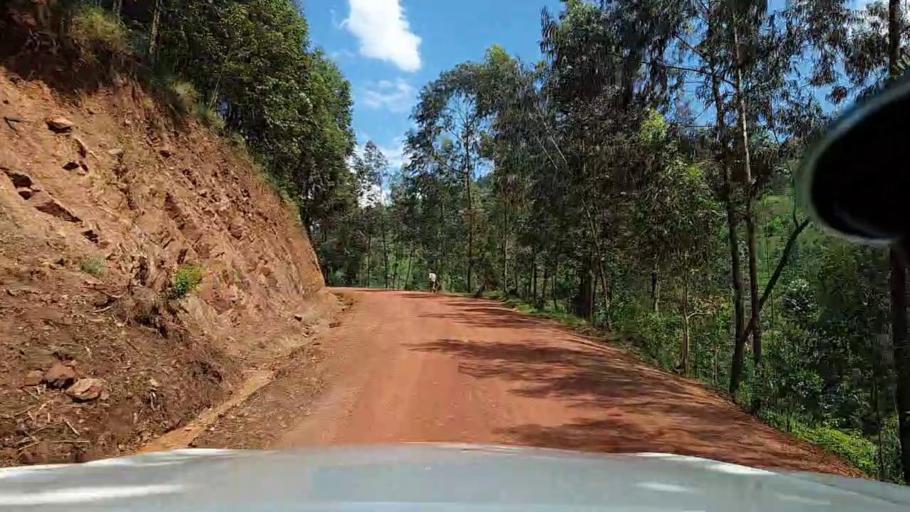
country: RW
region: Northern Province
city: Byumba
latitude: -1.7454
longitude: 29.8630
